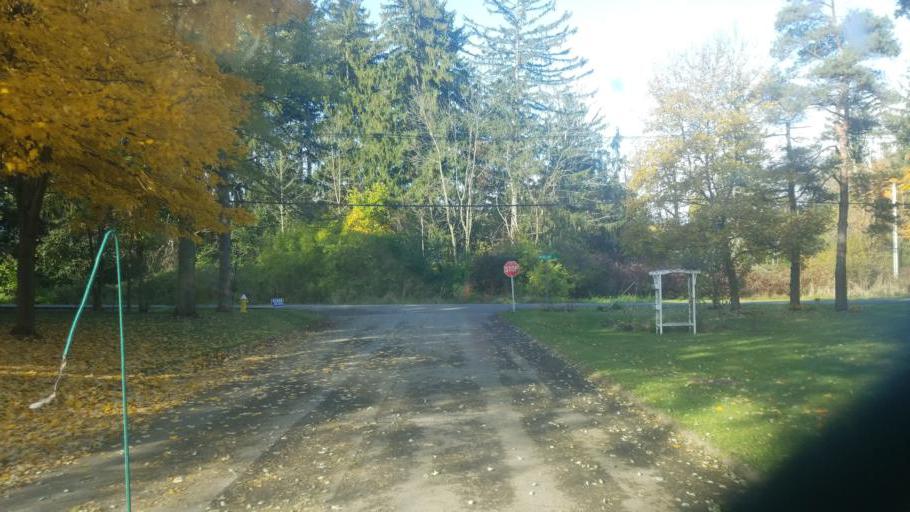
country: US
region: Ohio
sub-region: Richland County
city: Mansfield
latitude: 40.7368
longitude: -82.5417
